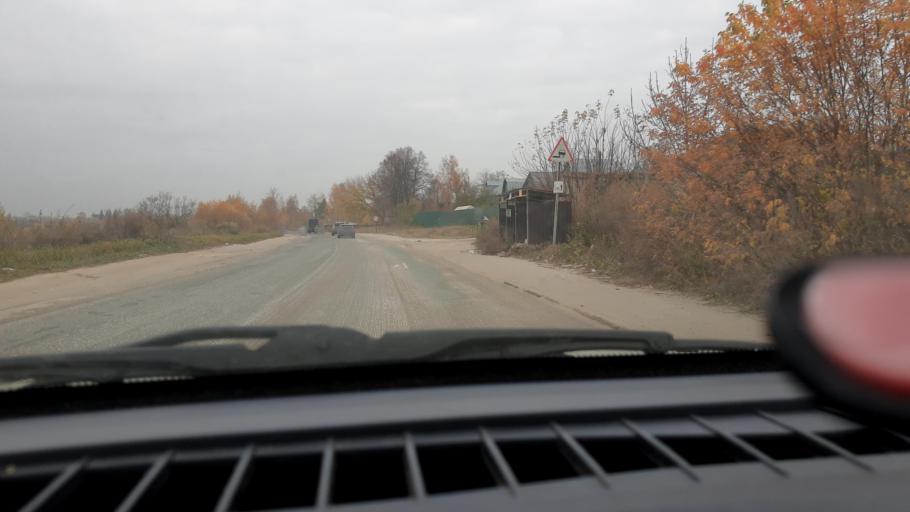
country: RU
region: Nizjnij Novgorod
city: Neklyudovo
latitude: 56.4126
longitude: 43.9743
